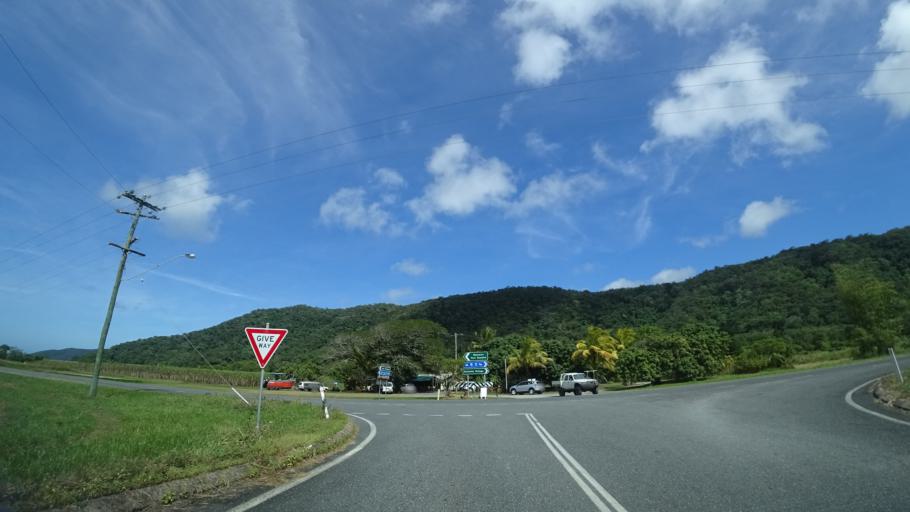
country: AU
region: Queensland
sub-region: Cairns
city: Port Douglas
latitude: -16.2840
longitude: 145.3793
